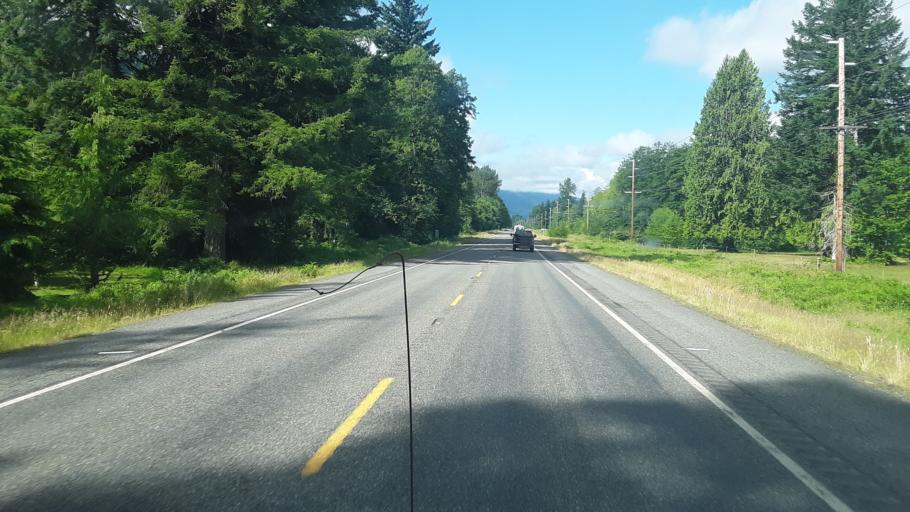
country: US
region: Washington
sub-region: Lewis County
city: Morton
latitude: 46.5616
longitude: -121.7185
